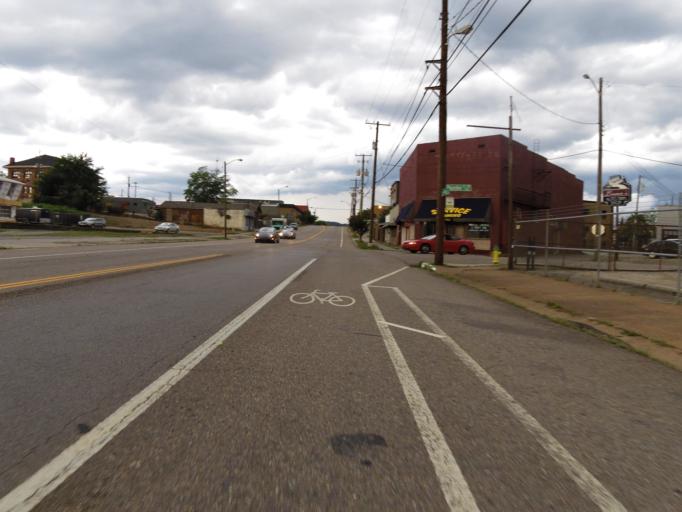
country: US
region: Tennessee
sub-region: Knox County
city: Knoxville
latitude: 35.9780
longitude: -83.9257
